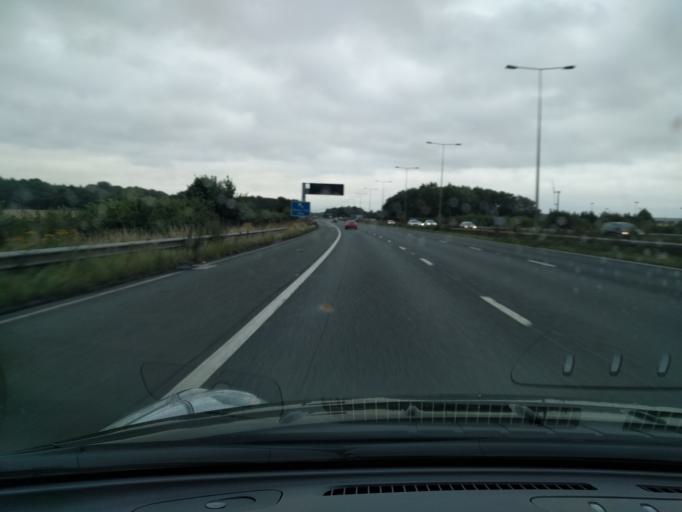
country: GB
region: England
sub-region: Borough of Wigan
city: Ashton in Makerfield
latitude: 53.4664
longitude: -2.6280
